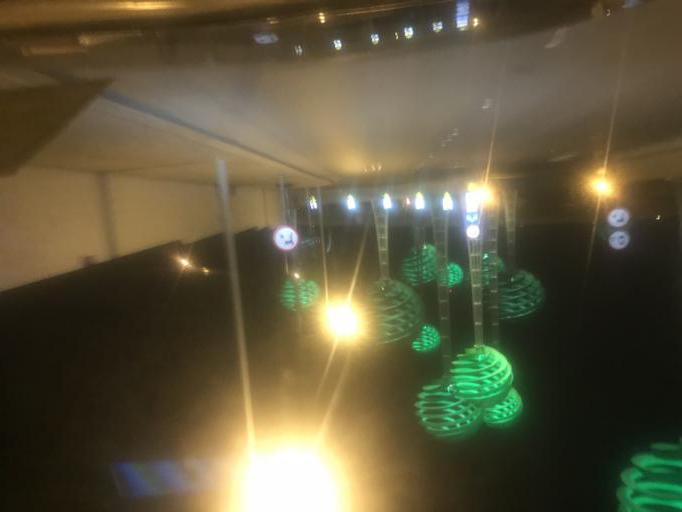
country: SA
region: Ar Riyad
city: Riyadh
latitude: 24.7043
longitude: 46.6224
